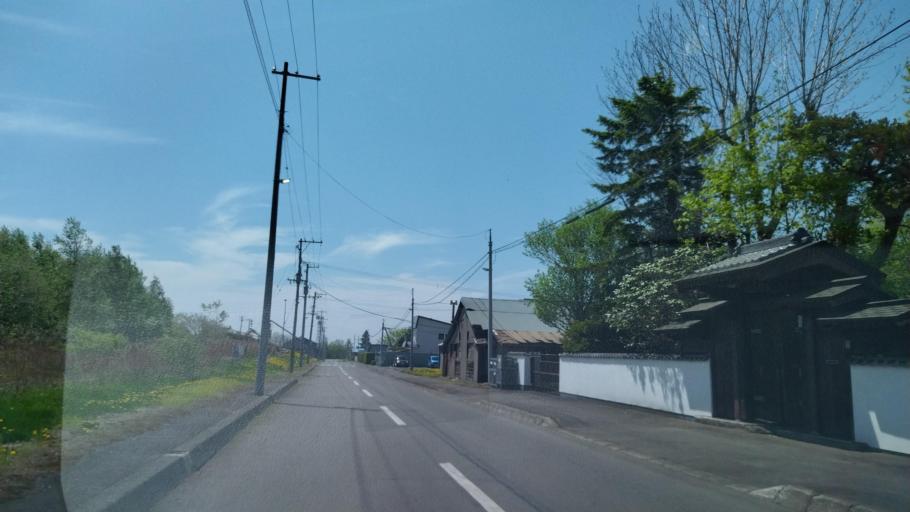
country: JP
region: Hokkaido
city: Otofuke
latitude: 43.2317
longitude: 143.2878
